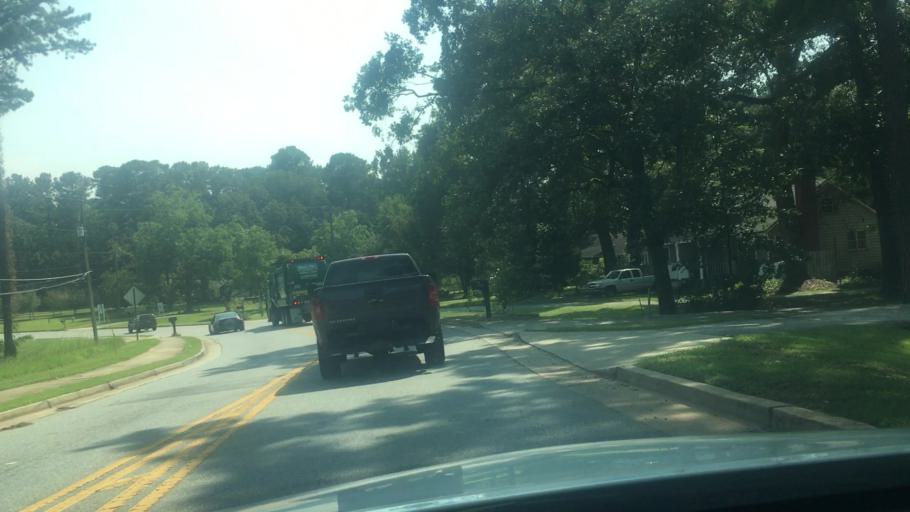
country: US
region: Georgia
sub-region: Gwinnett County
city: Lilburn
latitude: 33.8918
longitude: -84.1825
